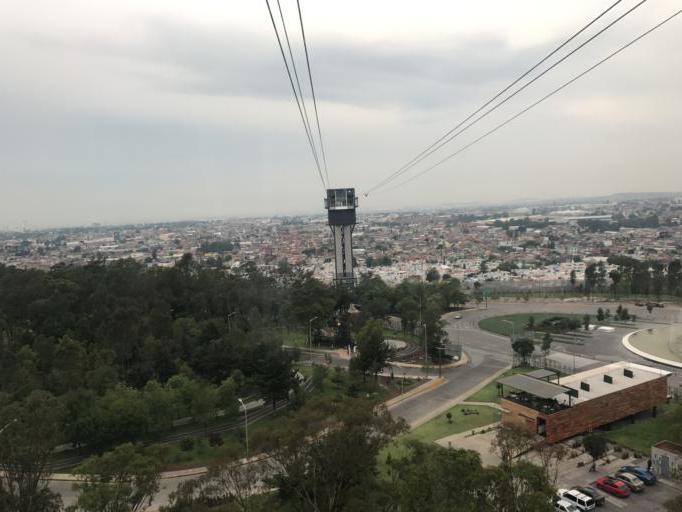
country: MX
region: Puebla
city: Puebla
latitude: 19.0590
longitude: -98.1840
